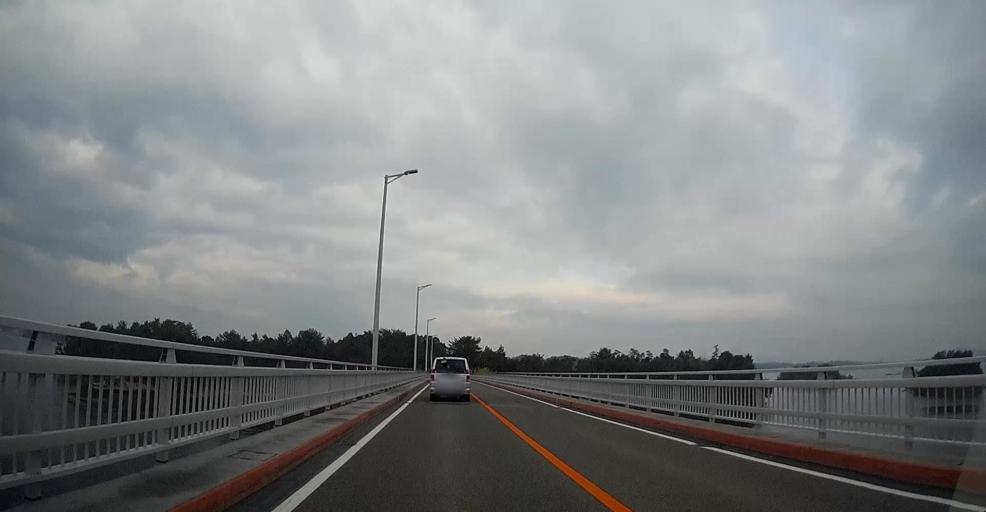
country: JP
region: Kumamoto
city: Yatsushiro
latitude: 32.5300
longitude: 130.4243
